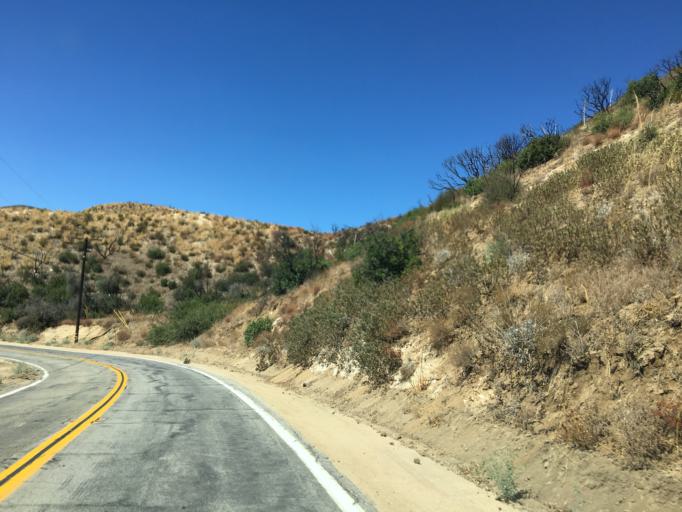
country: US
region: California
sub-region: Los Angeles County
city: Green Valley
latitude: 34.6585
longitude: -118.4625
